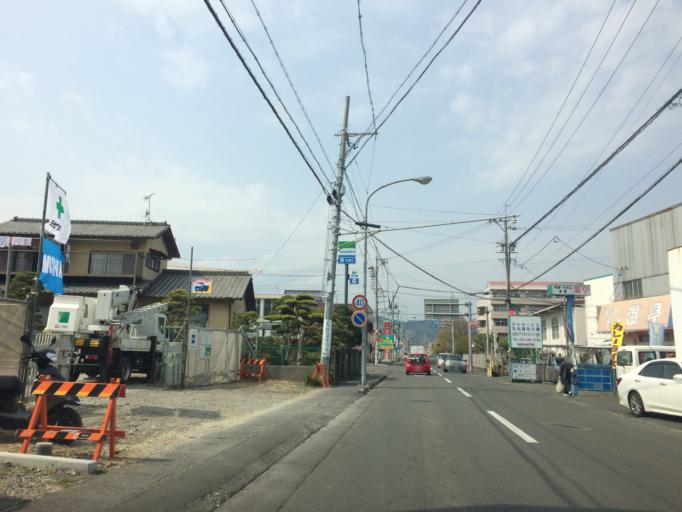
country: JP
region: Shizuoka
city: Shizuoka-shi
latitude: 34.9914
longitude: 138.3991
